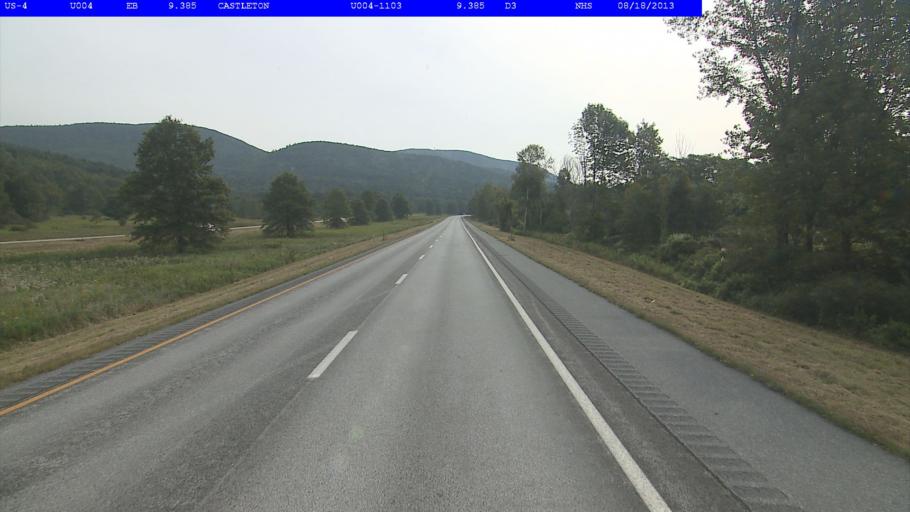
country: US
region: Vermont
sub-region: Rutland County
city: Castleton
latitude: 43.6159
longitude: -73.1347
